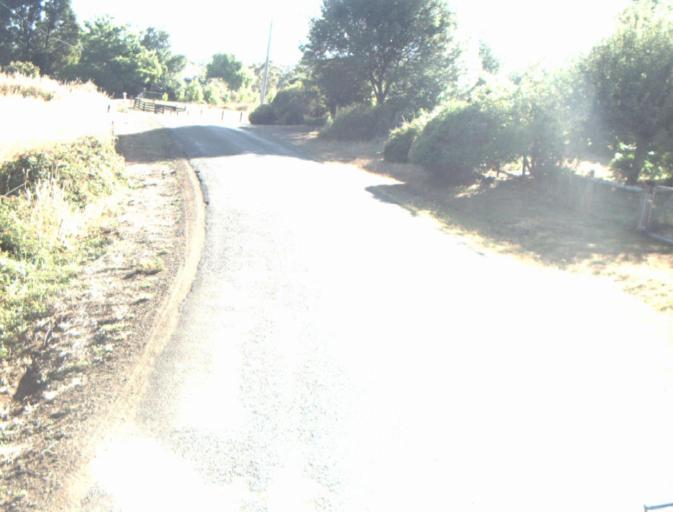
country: AU
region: Tasmania
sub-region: Launceston
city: Mayfield
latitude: -41.2950
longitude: 147.2029
